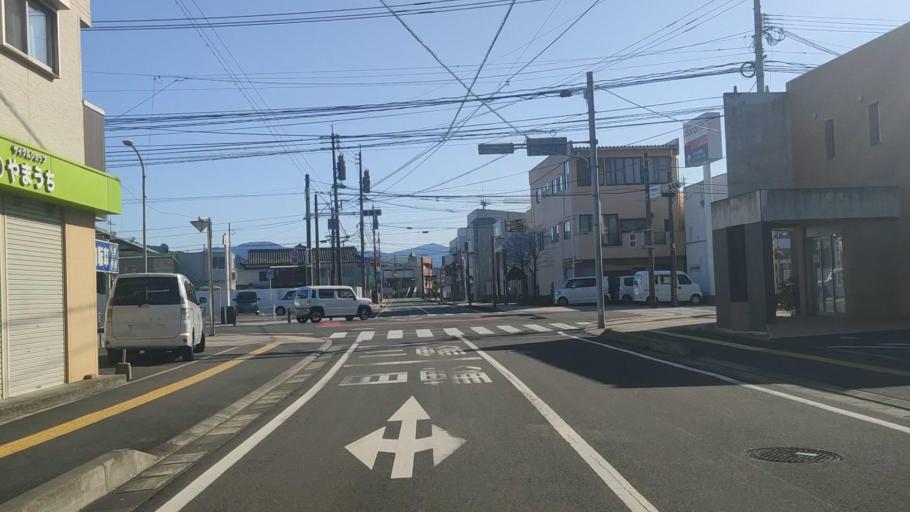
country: JP
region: Oita
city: Saiki
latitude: 32.9597
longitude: 131.8968
